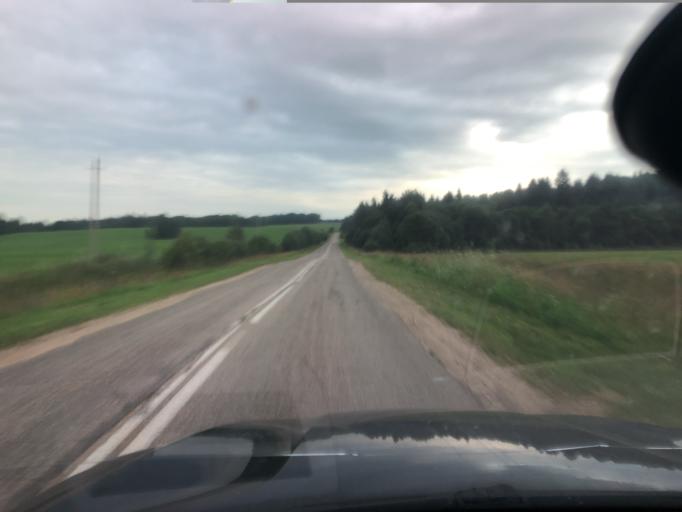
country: RU
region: Jaroslavl
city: Pereslavl'-Zalesskiy
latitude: 57.0217
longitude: 38.9449
